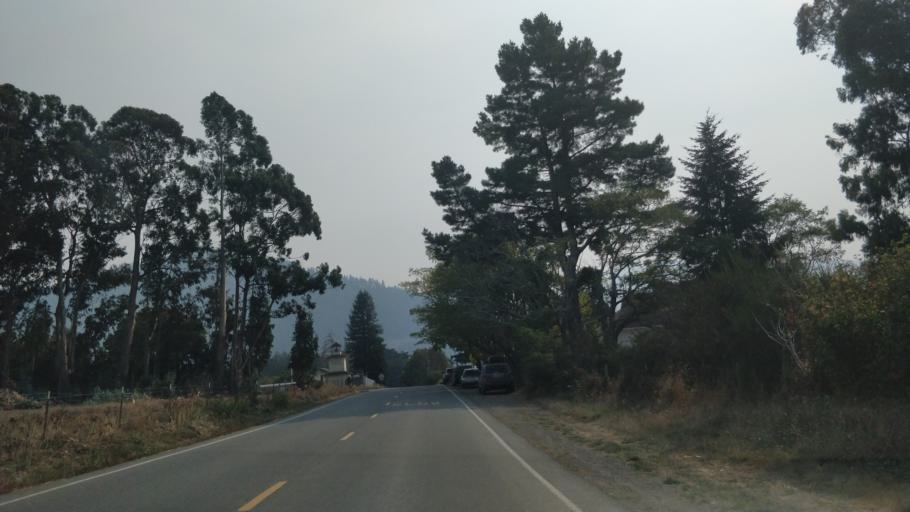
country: US
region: California
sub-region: Humboldt County
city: Rio Dell
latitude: 40.3234
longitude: -124.2858
